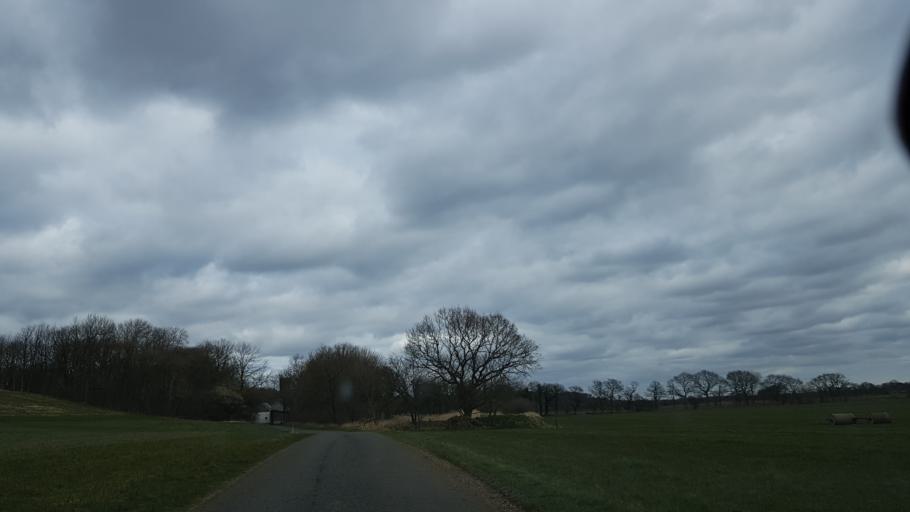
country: DK
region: South Denmark
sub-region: Vejen Kommune
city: Brorup
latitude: 55.4436
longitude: 8.9580
